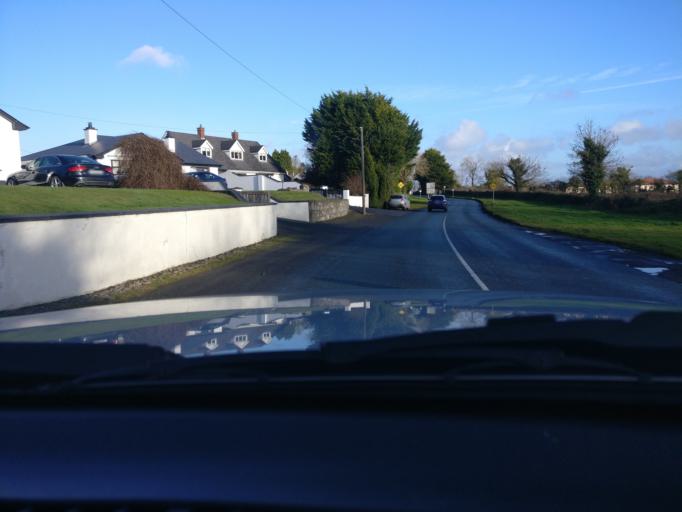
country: IE
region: Leinster
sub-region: An Iarmhi
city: An Muileann gCearr
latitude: 53.5157
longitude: -7.3784
